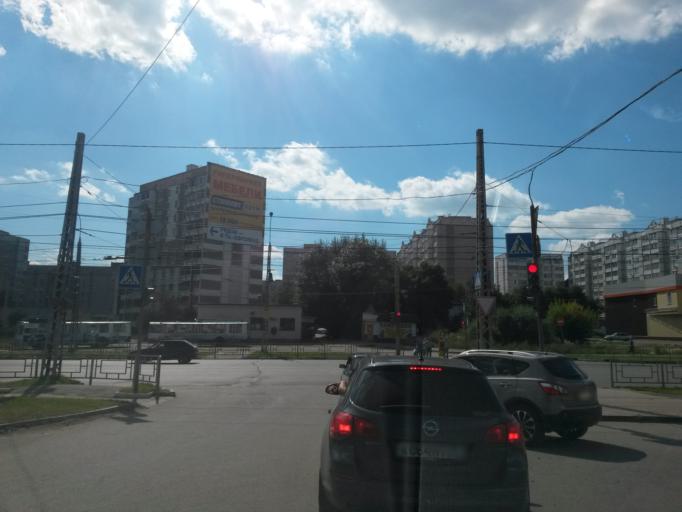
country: RU
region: Ivanovo
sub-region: Gorod Ivanovo
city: Ivanovo
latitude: 56.9628
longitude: 41.0265
